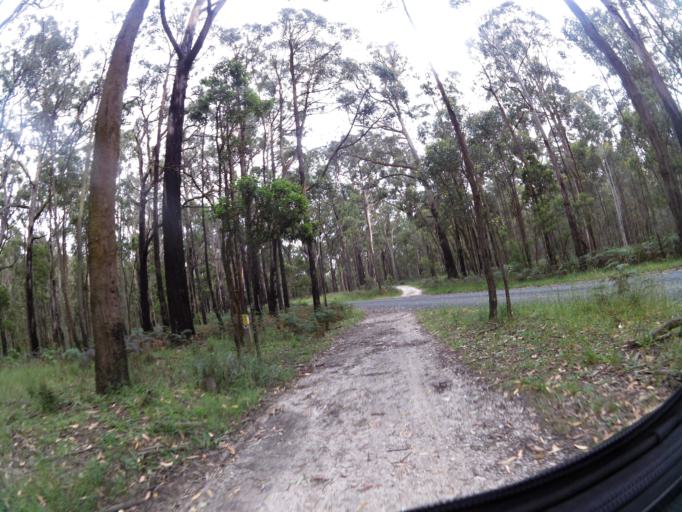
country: AU
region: Victoria
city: Brown Hill
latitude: -37.5054
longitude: 143.9081
